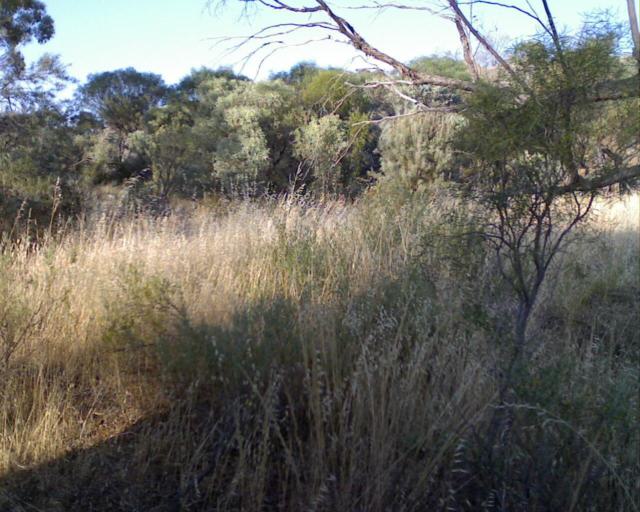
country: AU
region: Western Australia
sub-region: Merredin
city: Merredin
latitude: -30.8381
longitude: 117.9028
